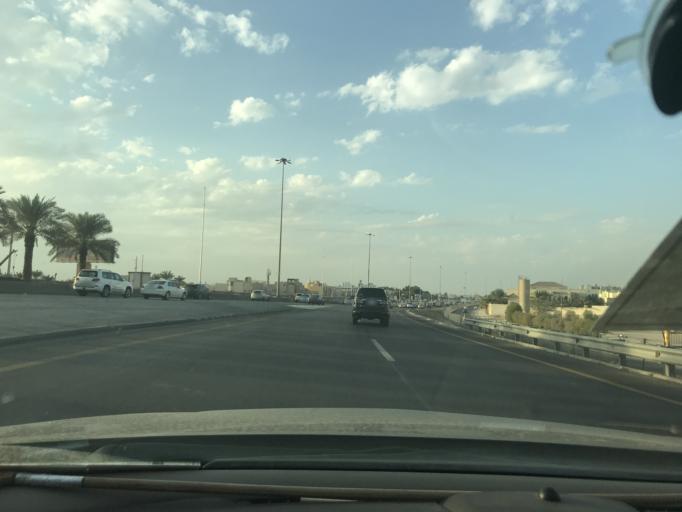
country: SA
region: Ar Riyad
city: Riyadh
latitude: 24.7398
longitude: 46.5886
